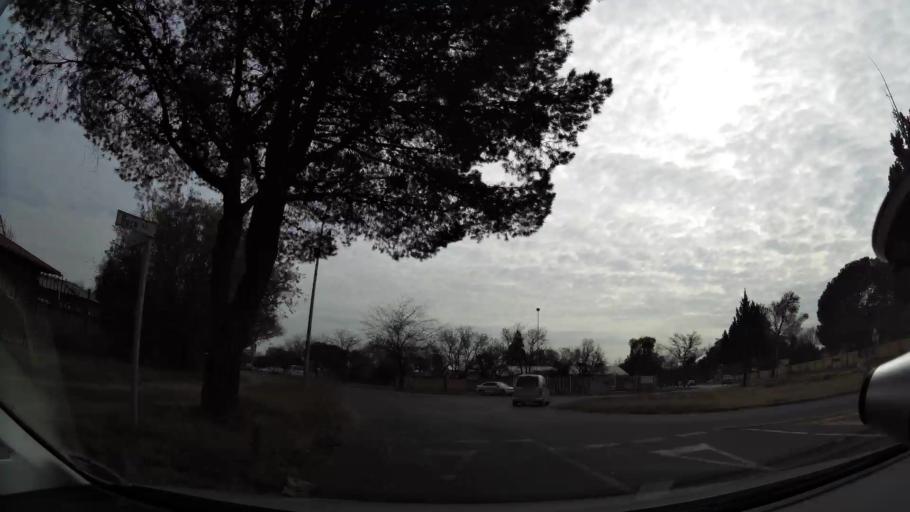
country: ZA
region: Orange Free State
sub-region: Mangaung Metropolitan Municipality
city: Bloemfontein
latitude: -29.1276
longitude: 26.2019
